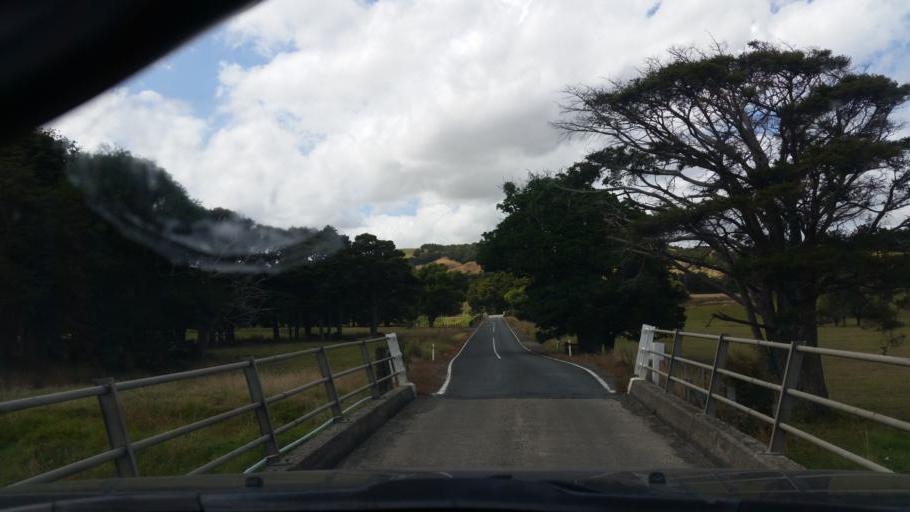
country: NZ
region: Northland
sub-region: Kaipara District
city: Dargaville
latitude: -35.8562
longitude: 173.8505
